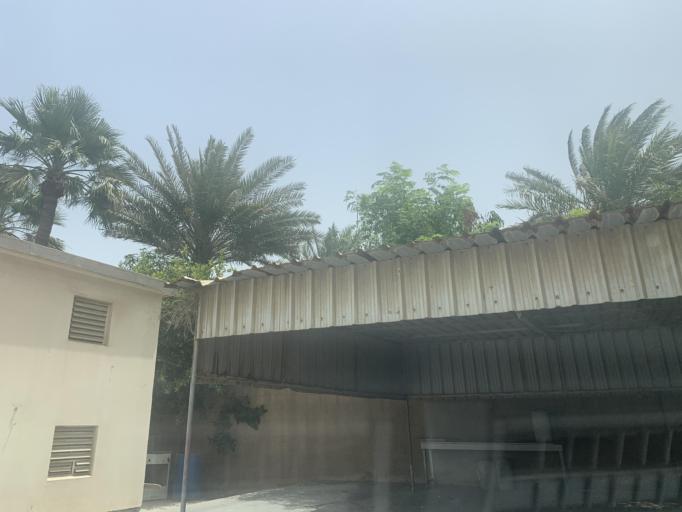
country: BH
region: Manama
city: Jidd Hafs
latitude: 26.2085
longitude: 50.5391
